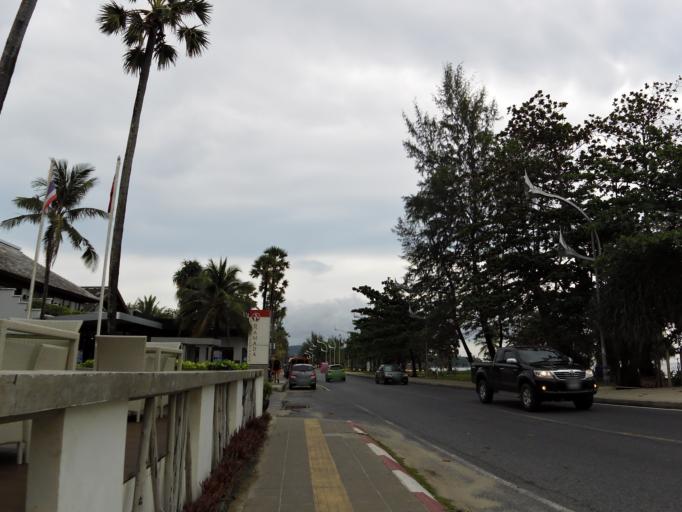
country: TH
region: Phuket
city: Ban Karon
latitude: 7.8471
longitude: 98.2935
